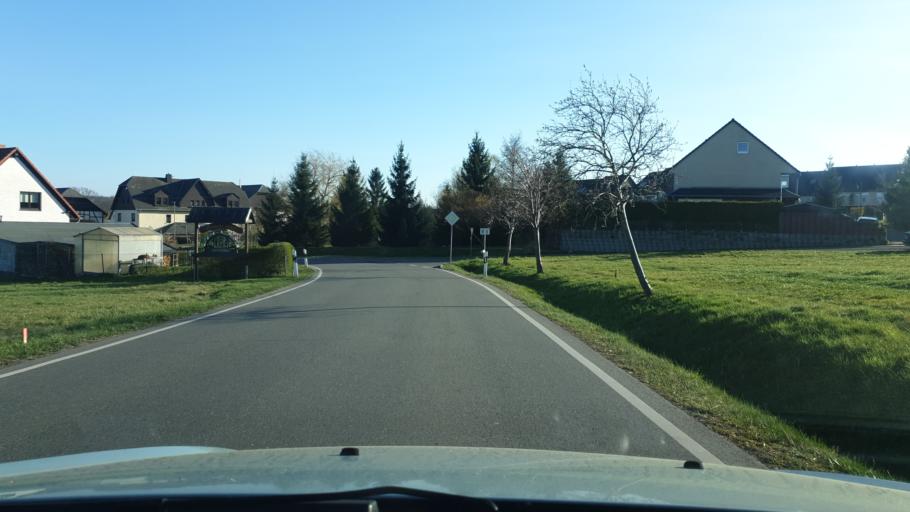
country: DE
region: Saxony
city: Niederdorf
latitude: 50.7665
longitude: 12.8018
